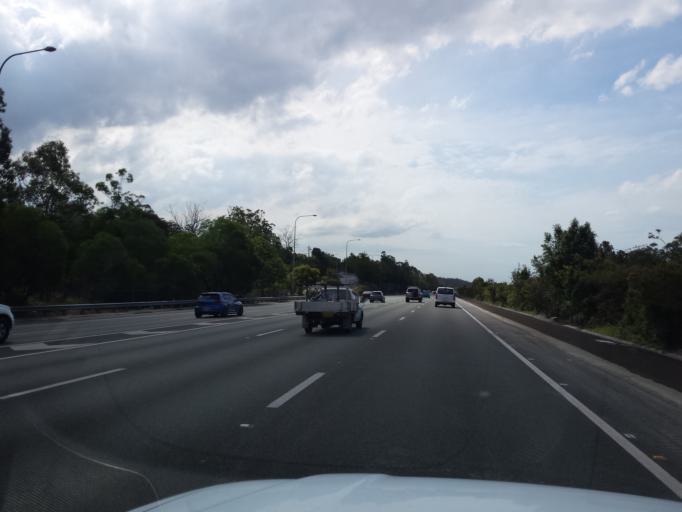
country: AU
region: Queensland
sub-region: Gold Coast
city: Nerang
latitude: -27.9505
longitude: 153.3421
